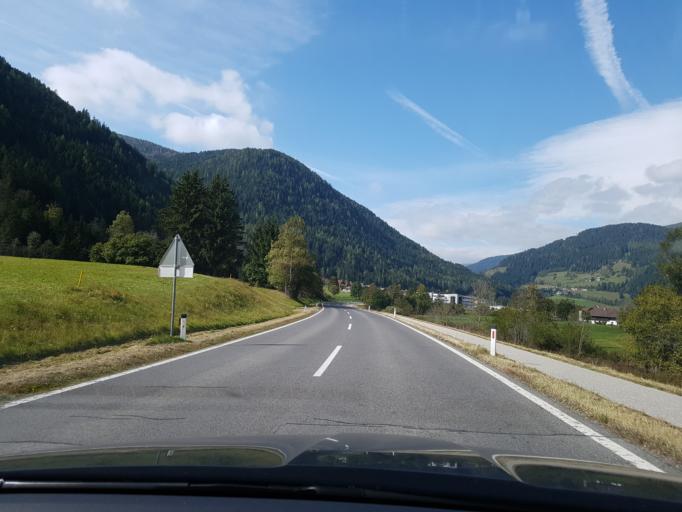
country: AT
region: Carinthia
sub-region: Politischer Bezirk Villach Land
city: Arriach
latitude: 46.8089
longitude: 13.8790
